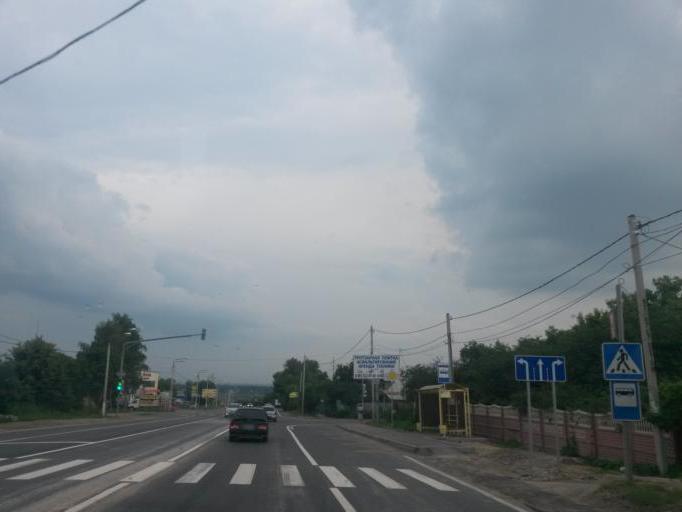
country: RU
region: Moskovskaya
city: Yam
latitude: 55.5057
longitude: 37.7527
